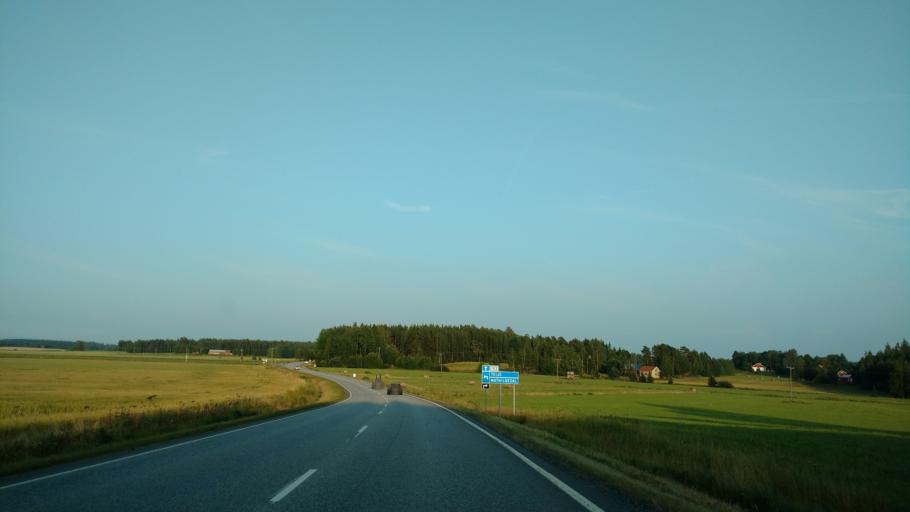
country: FI
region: Varsinais-Suomi
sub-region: Salo
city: Saerkisalo
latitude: 60.1747
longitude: 22.9576
